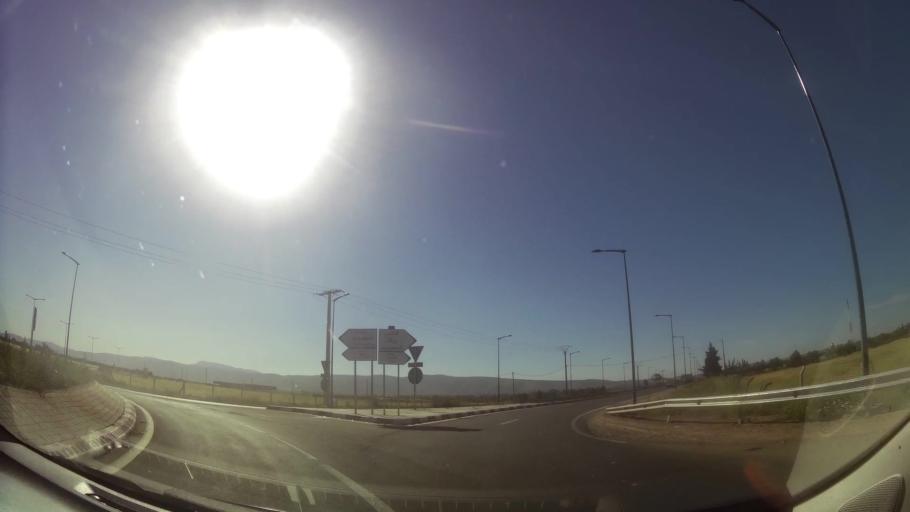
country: MA
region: Oriental
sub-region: Berkane-Taourirt
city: Ahfir
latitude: 34.8405
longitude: -1.9810
